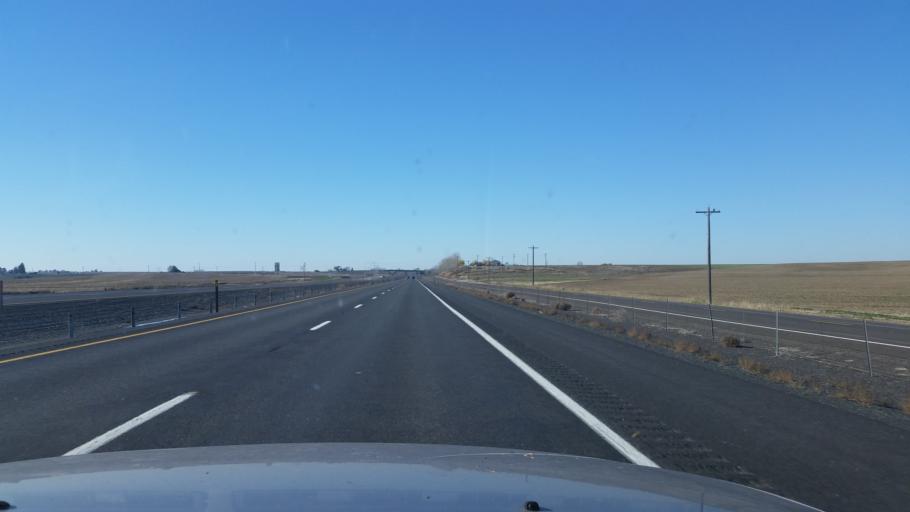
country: US
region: Washington
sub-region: Grant County
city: Warden
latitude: 47.0855
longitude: -119.0291
